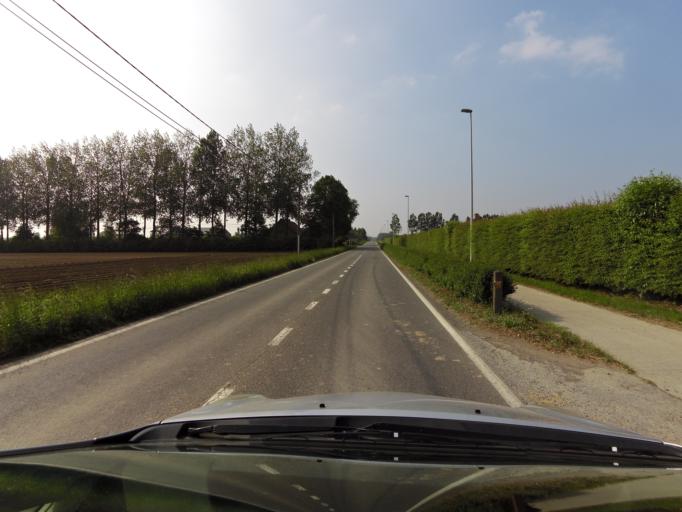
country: BE
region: Flanders
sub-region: Provincie West-Vlaanderen
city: Poperinge
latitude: 50.8662
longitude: 2.7163
